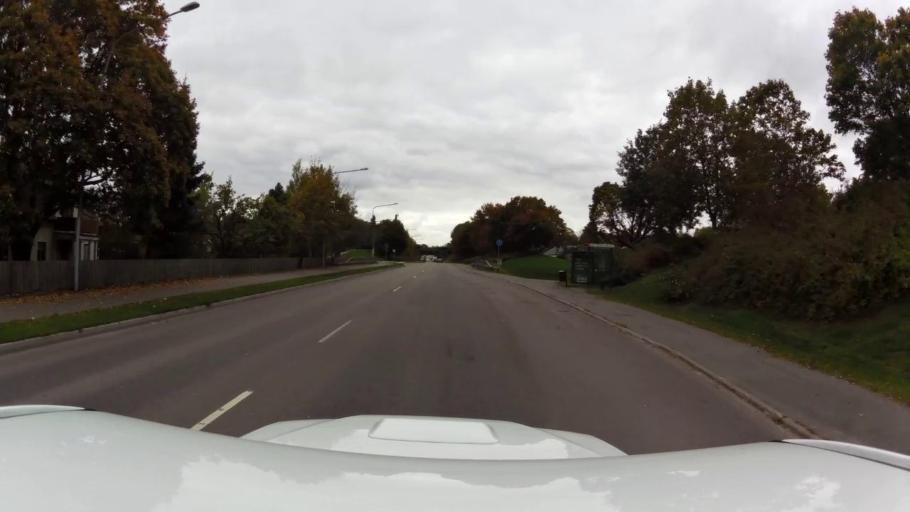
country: SE
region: OEstergoetland
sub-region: Linkopings Kommun
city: Ljungsbro
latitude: 58.5049
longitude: 15.5075
